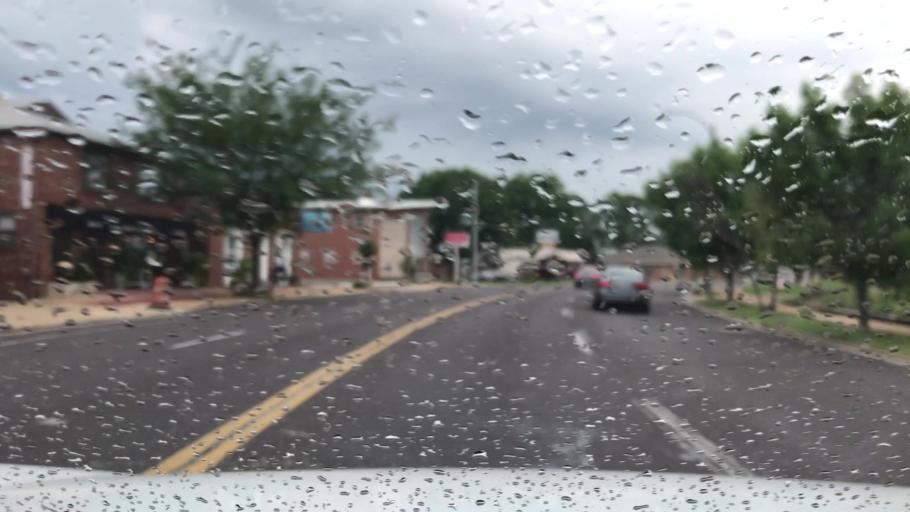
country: US
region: Missouri
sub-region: Saint Louis County
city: Maplewood
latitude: 38.5880
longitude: -90.2933
